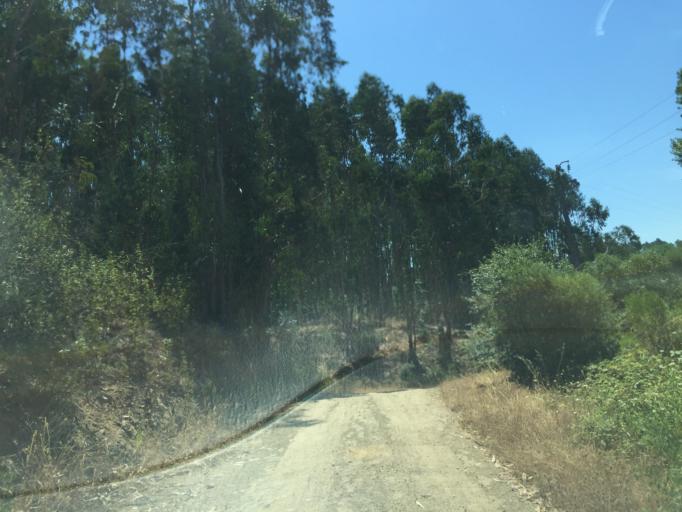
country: PT
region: Santarem
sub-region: Tomar
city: Tomar
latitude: 39.6006
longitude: -8.3570
